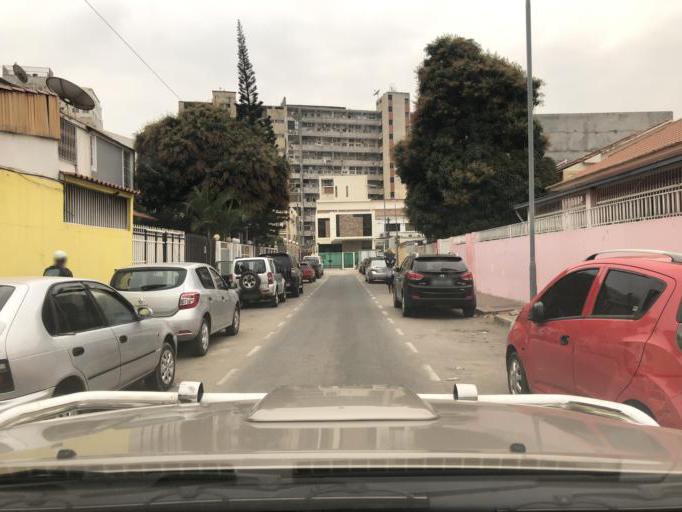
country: AO
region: Luanda
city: Luanda
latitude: -8.8200
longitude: 13.2485
